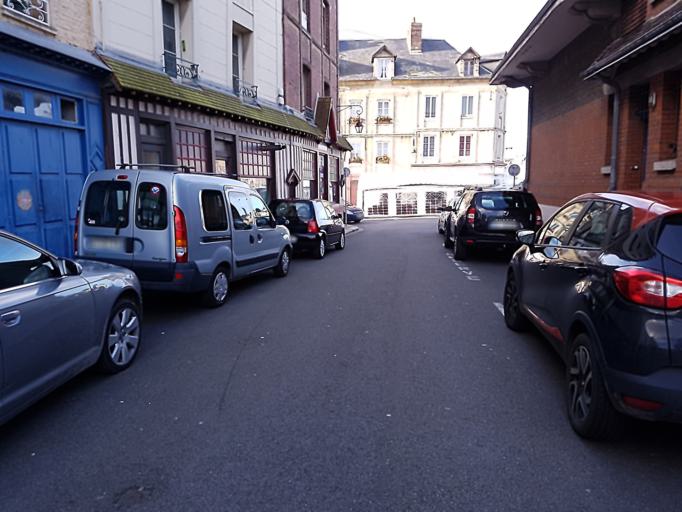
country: FR
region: Haute-Normandie
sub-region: Departement de la Seine-Maritime
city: Dieppe
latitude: 49.9271
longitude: 1.0841
